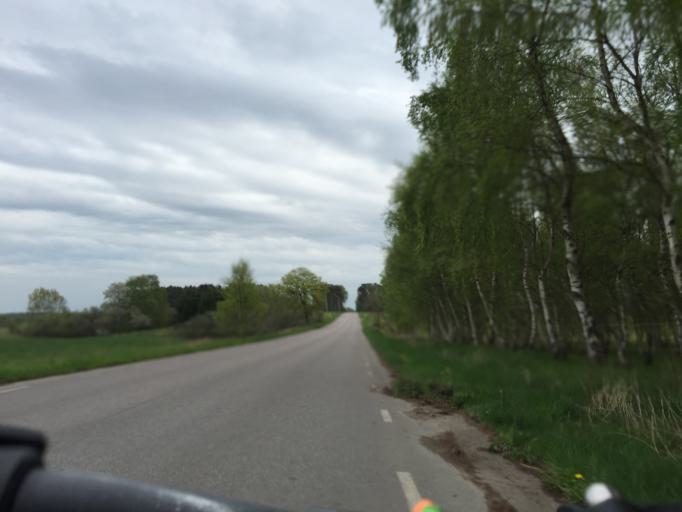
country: SE
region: Skane
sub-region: Lunds Kommun
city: Veberod
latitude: 55.6466
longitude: 13.4616
